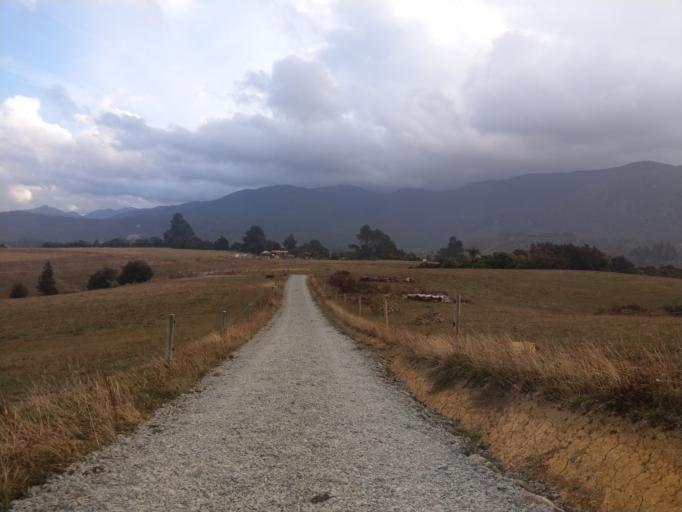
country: NZ
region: Tasman
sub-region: Tasman District
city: Takaka
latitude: -40.7905
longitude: 172.7446
